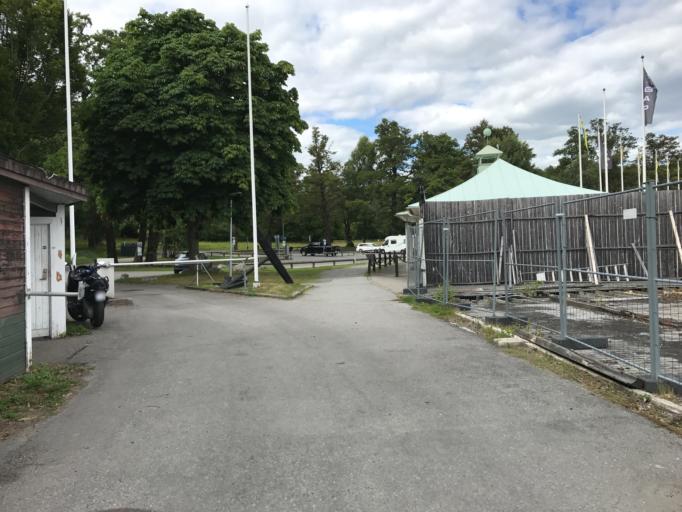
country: SE
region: Stockholm
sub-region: Nacka Kommun
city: Nacka
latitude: 59.3209
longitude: 18.1235
